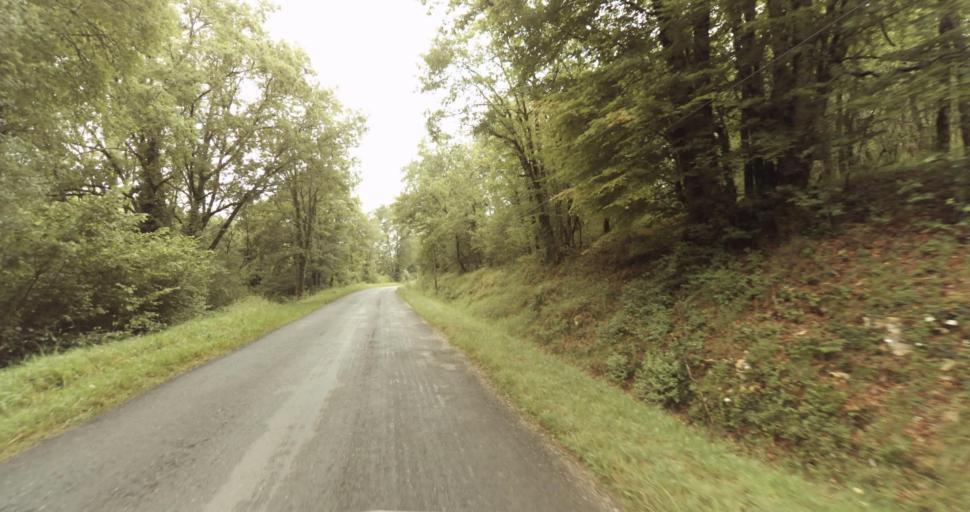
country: FR
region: Aquitaine
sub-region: Departement de la Dordogne
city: Lalinde
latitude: 44.8870
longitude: 0.7734
